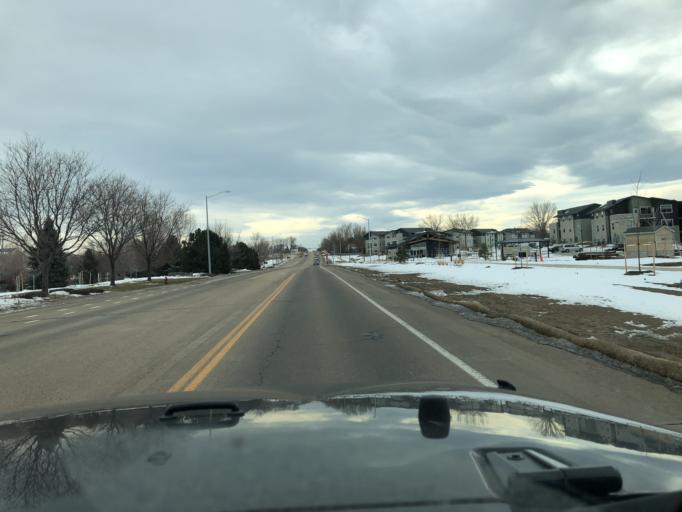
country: US
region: Colorado
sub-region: Boulder County
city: Longmont
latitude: 40.1807
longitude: -105.0742
